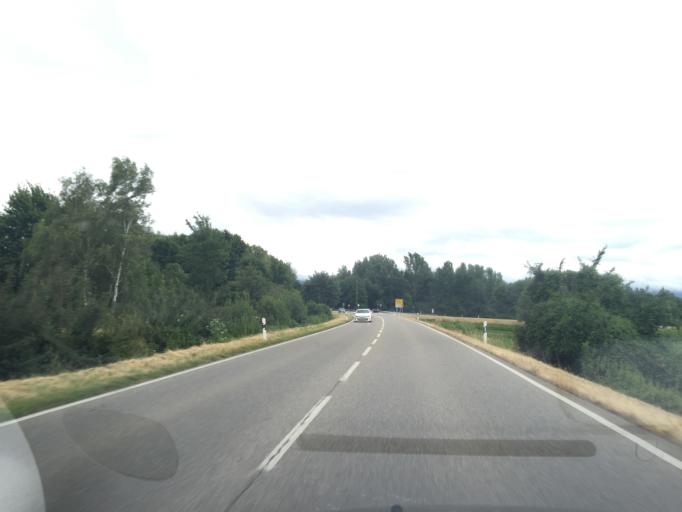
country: DE
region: Baden-Wuerttemberg
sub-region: Freiburg Region
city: Unterkrozingen
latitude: 47.9302
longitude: 7.6888
